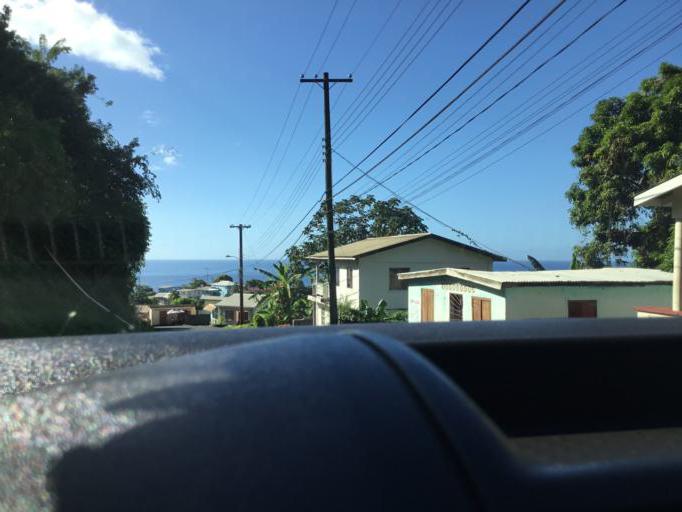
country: VC
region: Saint David
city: Chateaubelair
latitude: 13.2800
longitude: -61.2550
